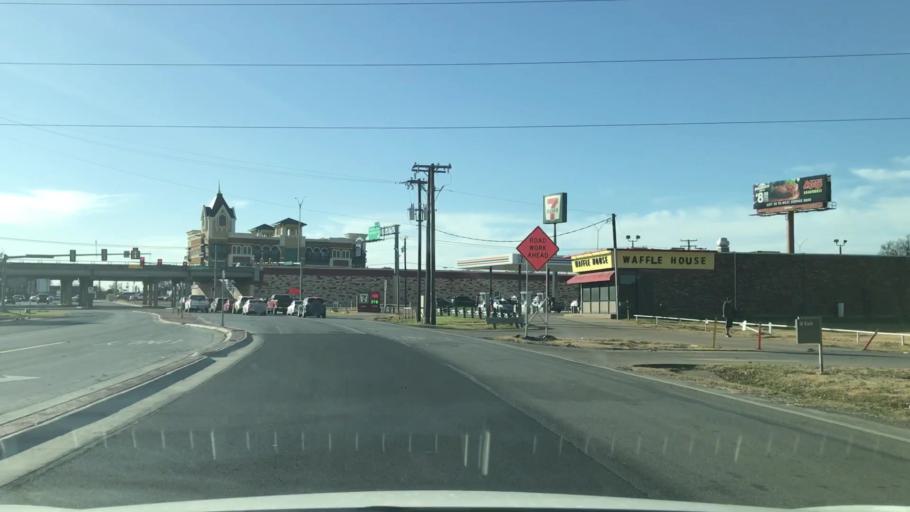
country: US
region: Texas
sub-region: Johnson County
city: Burleson
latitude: 32.5441
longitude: -97.3132
